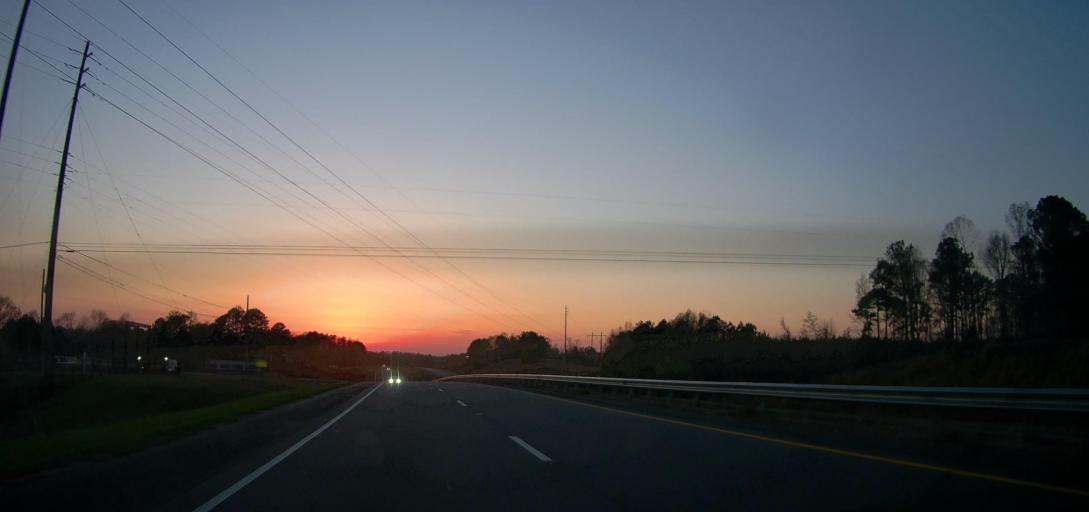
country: US
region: Alabama
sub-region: Tallapoosa County
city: Alexander City
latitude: 32.8850
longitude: -85.8607
